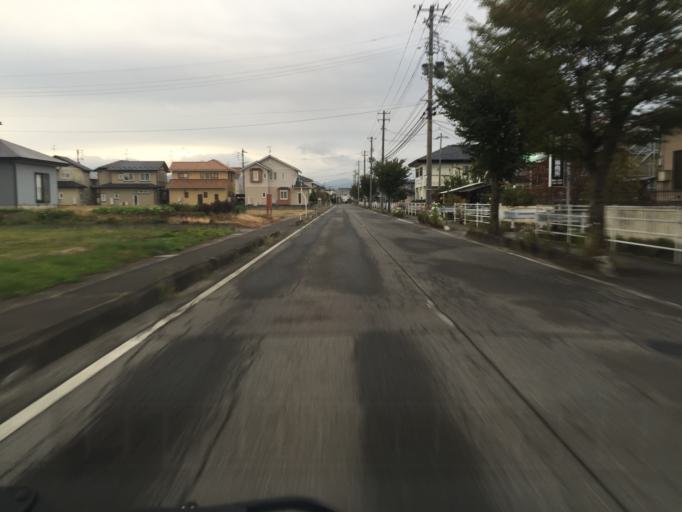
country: JP
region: Fukushima
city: Kitakata
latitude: 37.5193
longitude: 139.8751
